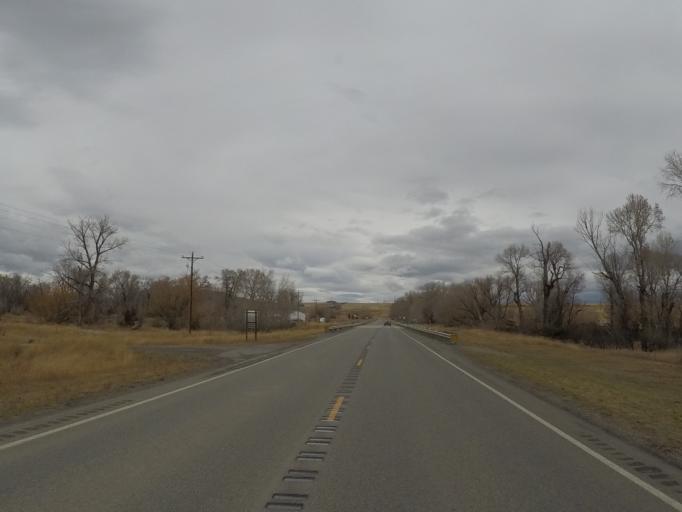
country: US
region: Montana
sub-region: Sweet Grass County
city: Big Timber
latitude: 45.8568
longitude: -109.9395
